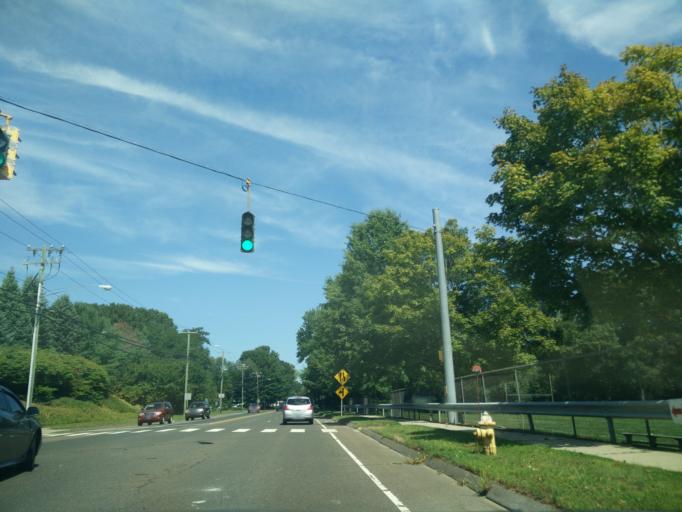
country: US
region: Connecticut
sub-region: Middlesex County
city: Clinton
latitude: 41.2929
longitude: -72.5308
